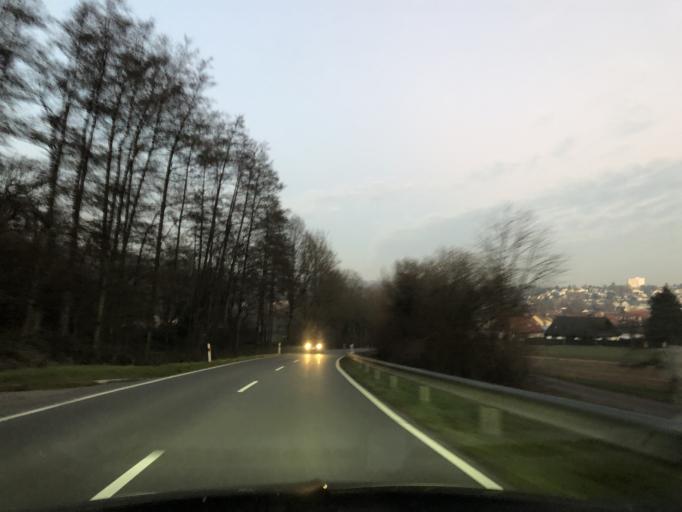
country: DE
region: Baden-Wuerttemberg
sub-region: Karlsruhe Region
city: Bammental
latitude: 49.3487
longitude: 8.7658
